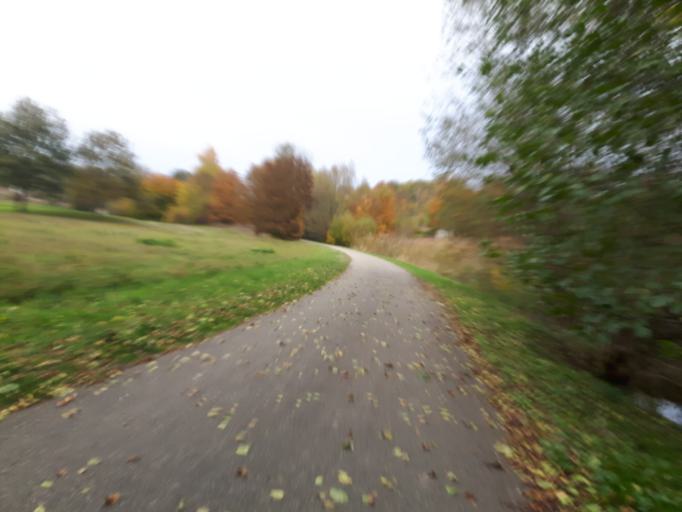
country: DE
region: Baden-Wuerttemberg
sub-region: Karlsruhe Region
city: Zaisenhausen
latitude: 49.1694
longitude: 8.7788
